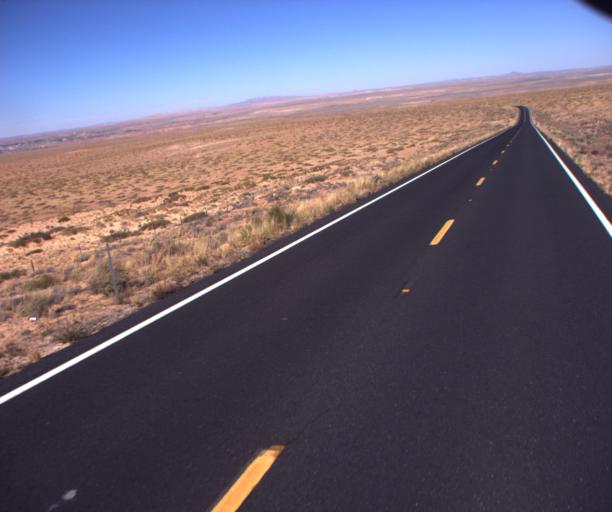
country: US
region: Arizona
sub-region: Coconino County
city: Tuba City
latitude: 36.0422
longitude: -111.1842
